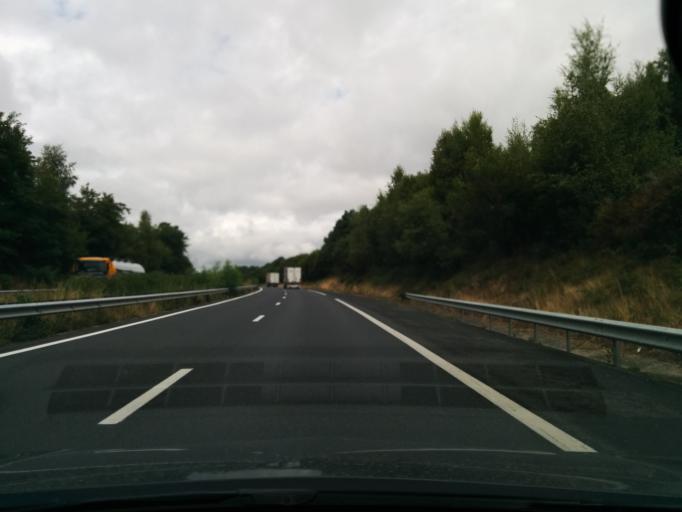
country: FR
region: Limousin
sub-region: Departement de la Correze
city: Uzerche
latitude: 45.3876
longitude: 1.5747
